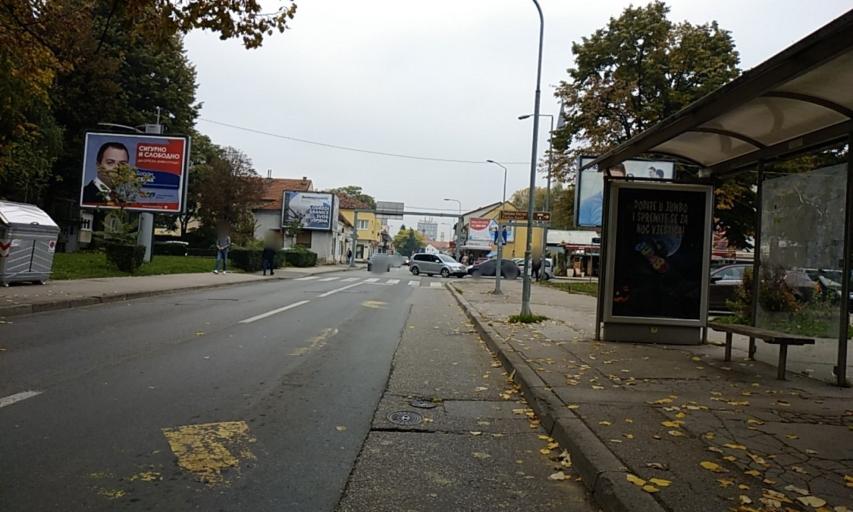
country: BA
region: Republika Srpska
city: Mejdan - Obilicevo
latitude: 44.7664
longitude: 17.1858
